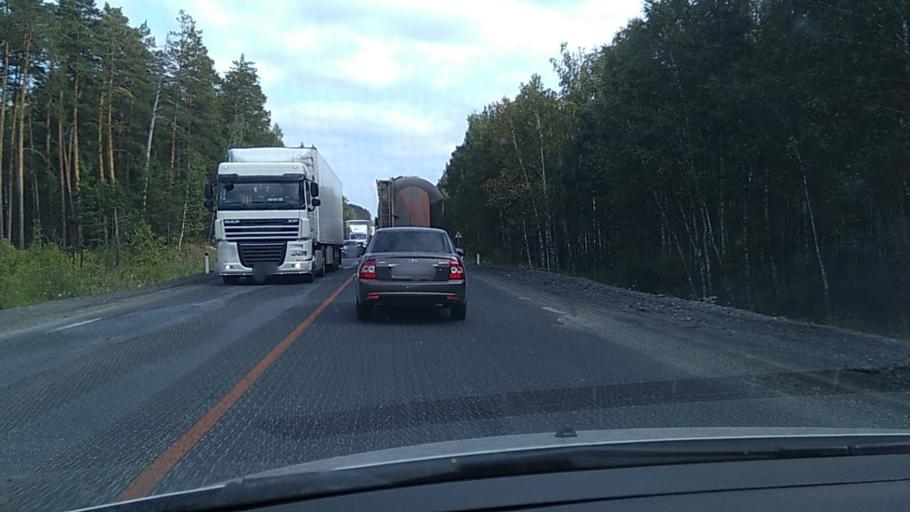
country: RU
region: Chelyabinsk
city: Miass
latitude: 54.9273
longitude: 60.2130
